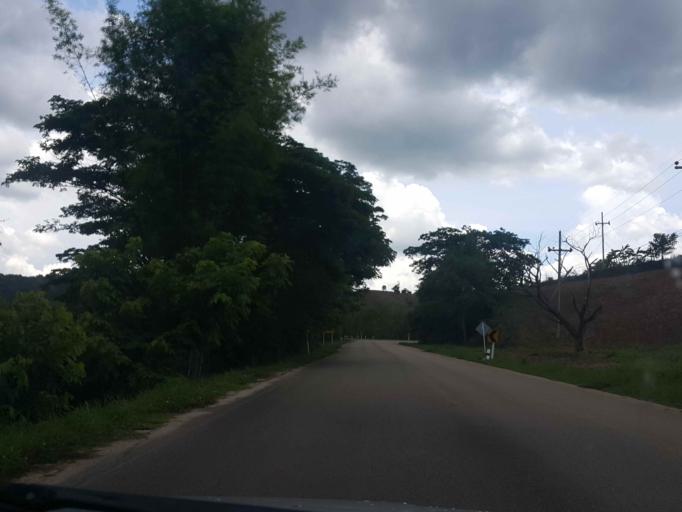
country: TH
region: Phayao
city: Dok Kham Tai
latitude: 18.9654
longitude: 100.0743
